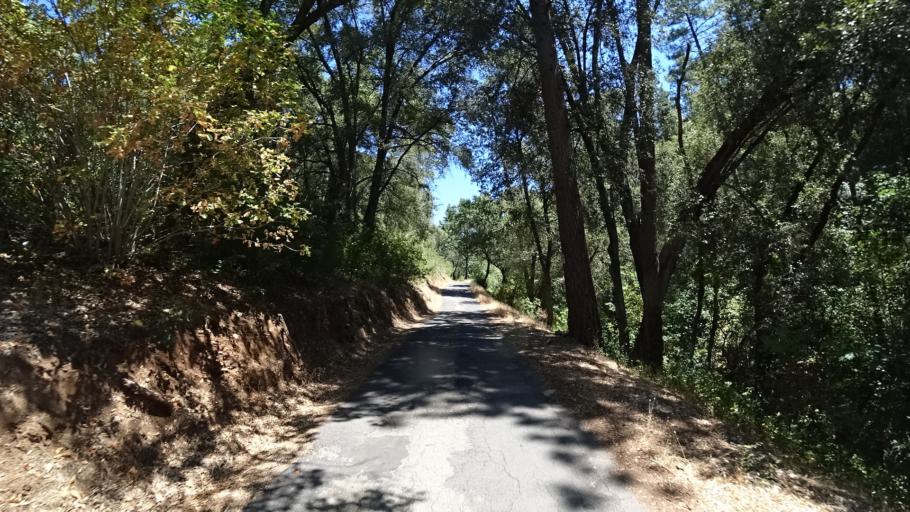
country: US
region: California
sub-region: Calaveras County
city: Forest Meadows
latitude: 38.1431
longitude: -120.4170
